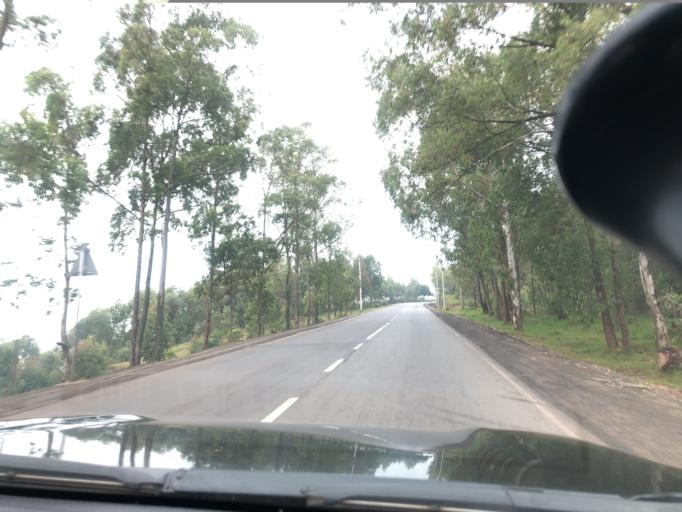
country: RW
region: Kigali
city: Kigali
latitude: -1.8159
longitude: 29.9405
